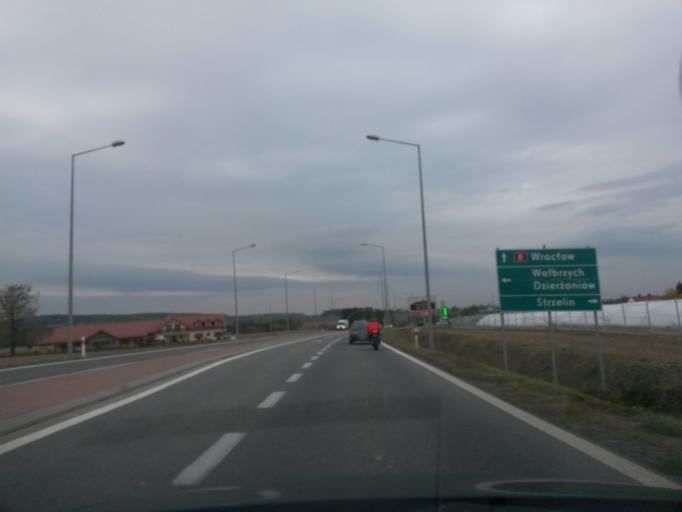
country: PL
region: Lower Silesian Voivodeship
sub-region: Powiat dzierzoniowski
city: Niemcza
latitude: 50.7196
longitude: 16.8249
